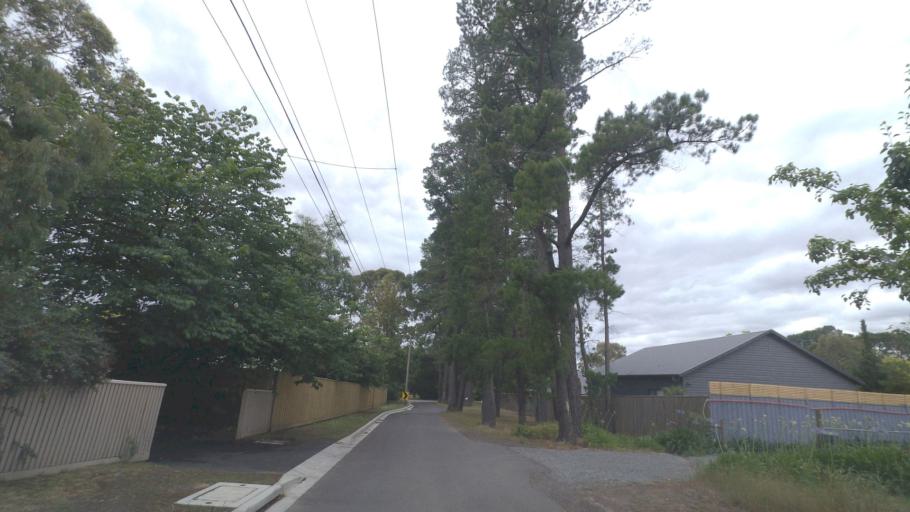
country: AU
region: Victoria
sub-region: Manningham
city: Park Orchards
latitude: -37.7791
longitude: 145.2235
